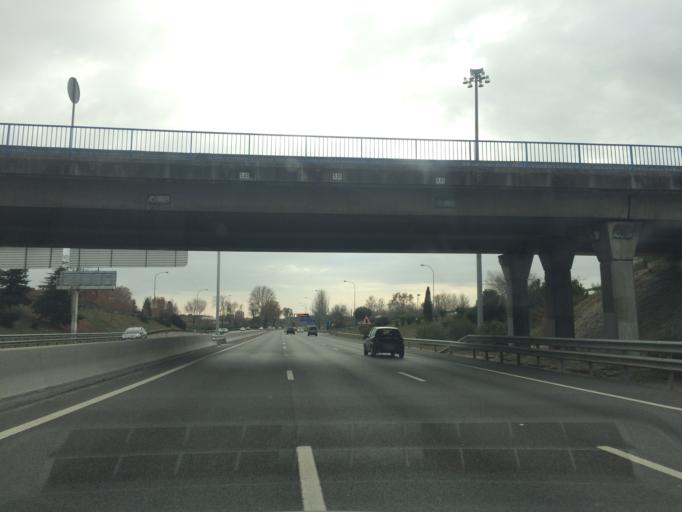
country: ES
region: Madrid
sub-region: Provincia de Madrid
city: Moncloa-Aravaca
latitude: 40.4452
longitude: -3.7398
